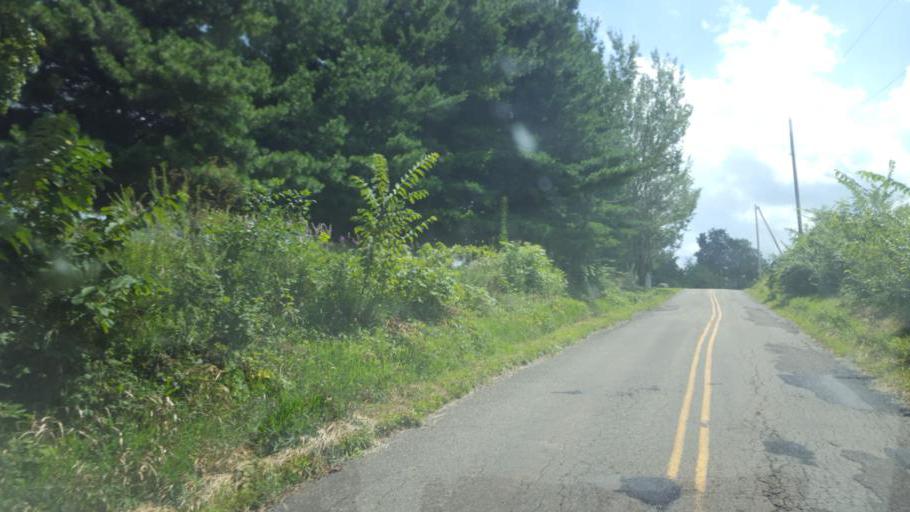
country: US
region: Ohio
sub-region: Knox County
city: Mount Vernon
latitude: 40.3842
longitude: -82.5825
